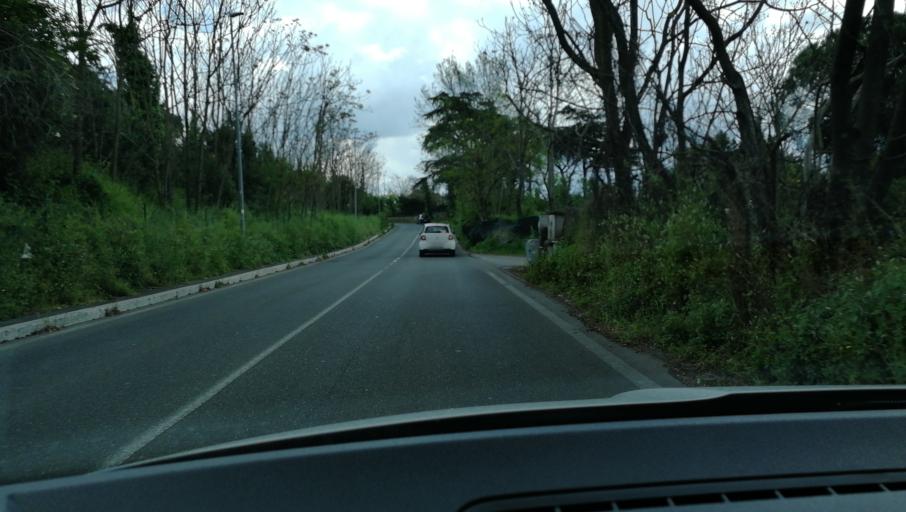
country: IT
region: Latium
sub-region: Citta metropolitana di Roma Capitale
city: Rome
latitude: 41.8608
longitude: 12.5354
